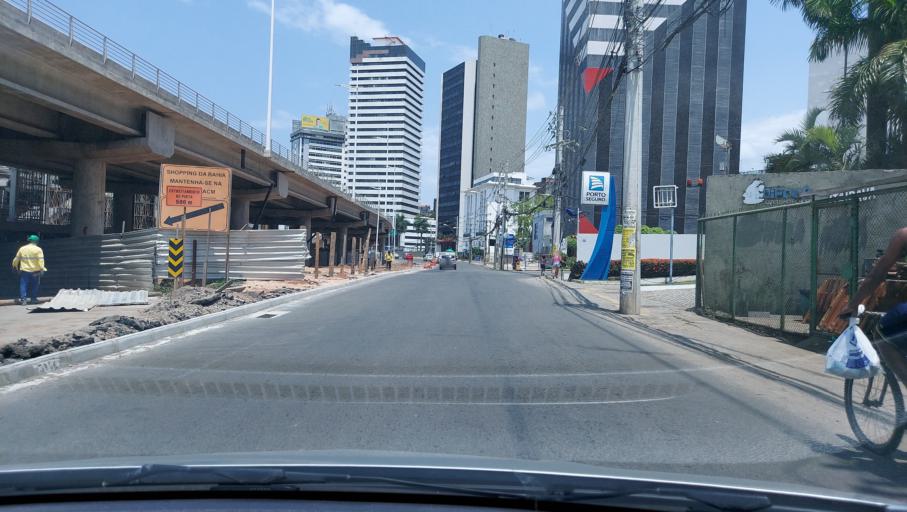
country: BR
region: Bahia
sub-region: Salvador
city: Salvador
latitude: -12.9888
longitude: -38.4711
